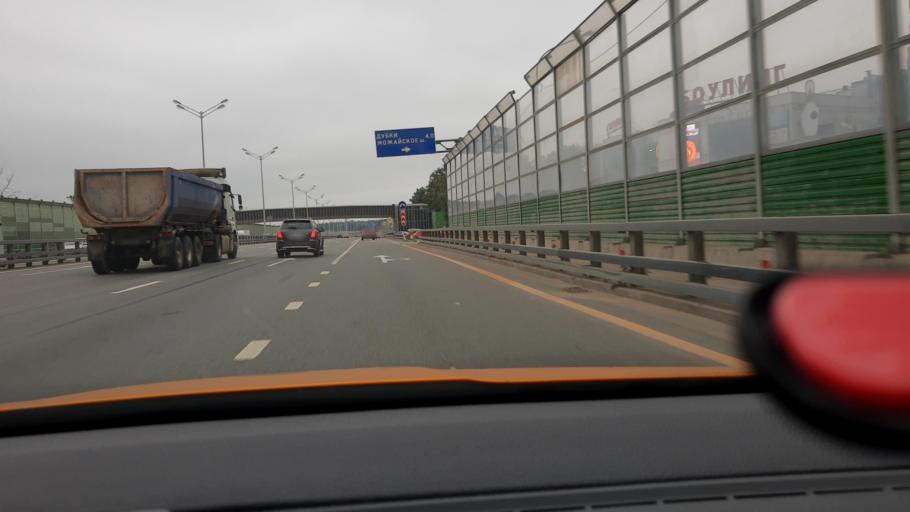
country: RU
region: Moskovskaya
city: Lesnoy Gorodok
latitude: 55.6326
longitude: 37.2144
